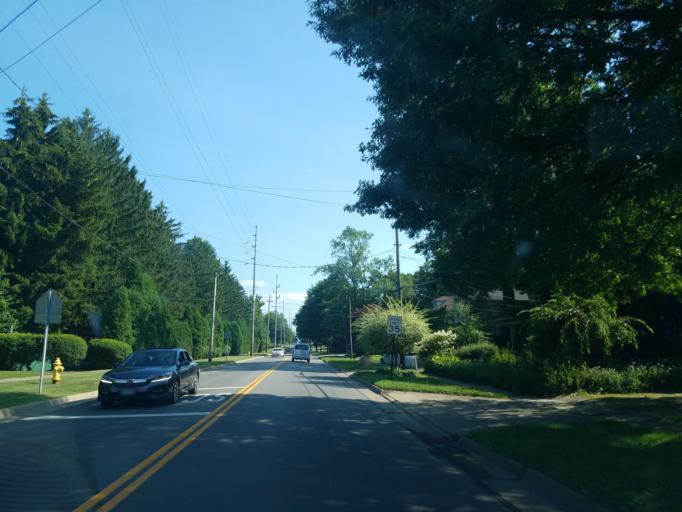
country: US
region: Ohio
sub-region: Summit County
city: Mogadore
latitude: 41.0463
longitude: -81.3931
